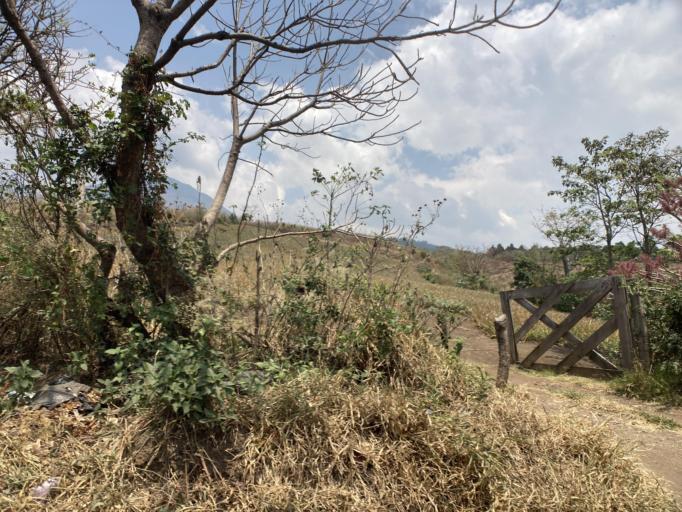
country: GT
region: Escuintla
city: San Vicente Pacaya
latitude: 14.3777
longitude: -90.5536
